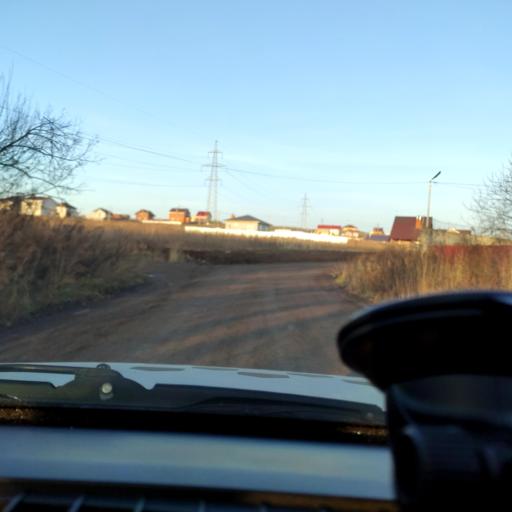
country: RU
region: Perm
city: Ferma
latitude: 57.9463
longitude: 56.3556
